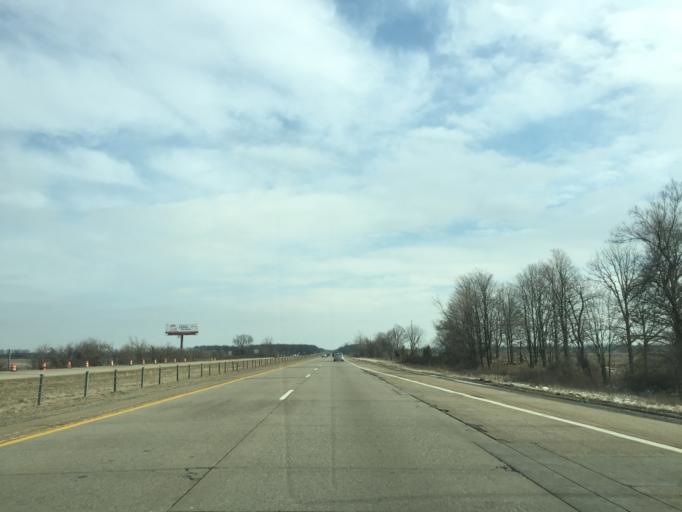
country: US
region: Michigan
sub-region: Ionia County
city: Ionia
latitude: 42.8790
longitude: -85.0288
